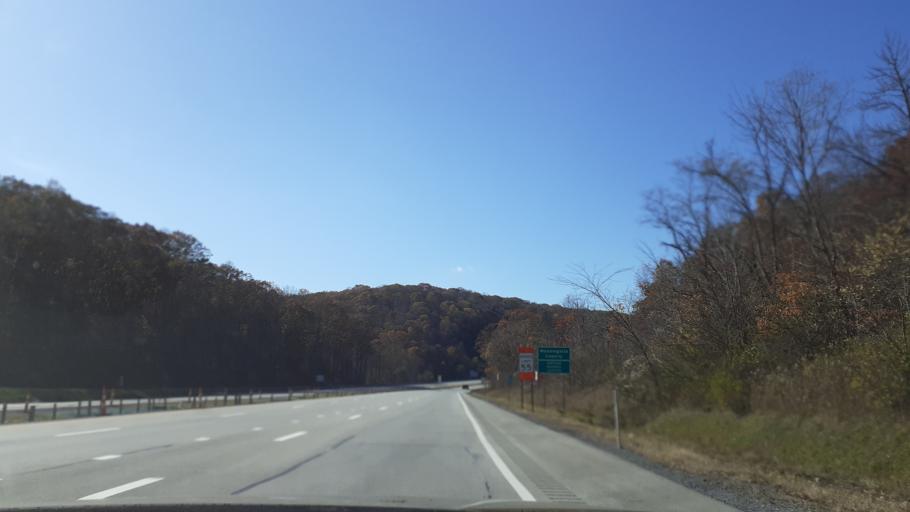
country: US
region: West Virginia
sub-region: Monongalia County
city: Cheat Lake
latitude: 39.6585
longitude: -79.7834
